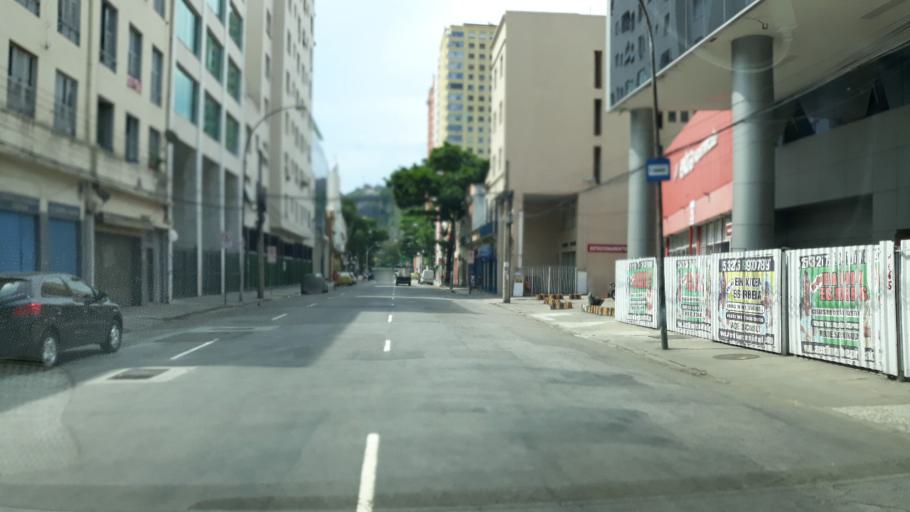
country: BR
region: Rio de Janeiro
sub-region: Rio De Janeiro
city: Rio de Janeiro
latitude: -22.9093
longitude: -43.1936
